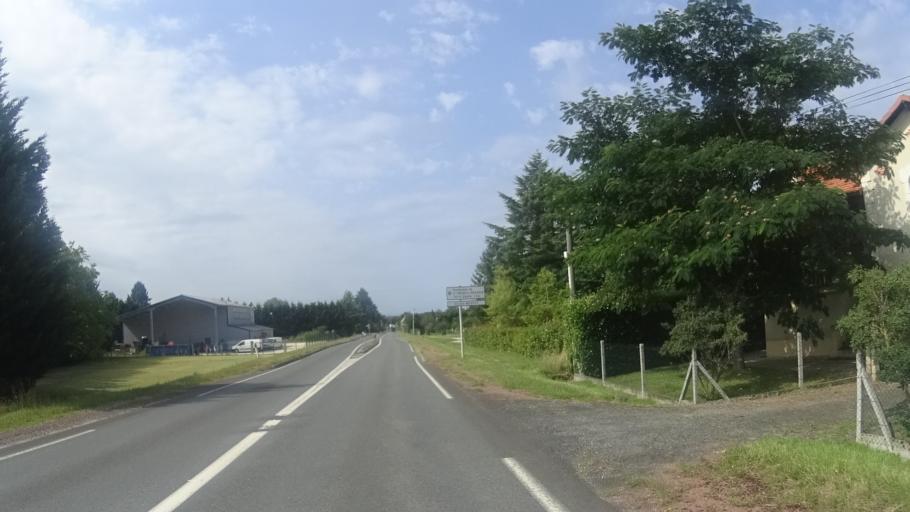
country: FR
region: Aquitaine
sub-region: Departement de la Dordogne
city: Mussidan
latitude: 45.0586
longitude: 0.3671
